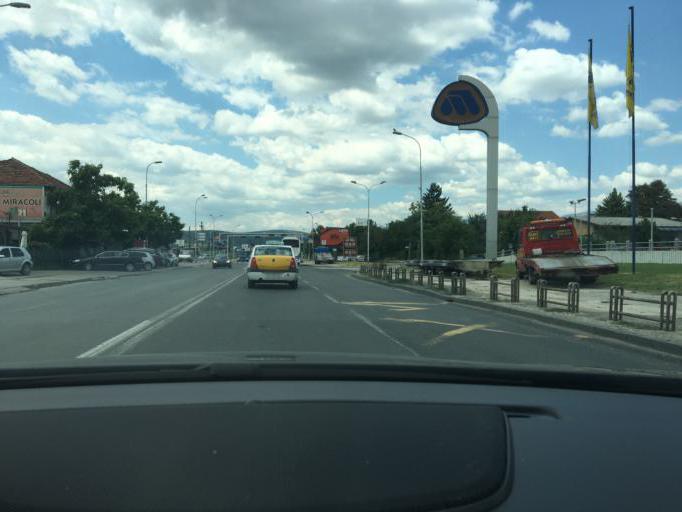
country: MK
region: Saraj
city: Saraj
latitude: 42.0069
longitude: 21.3345
